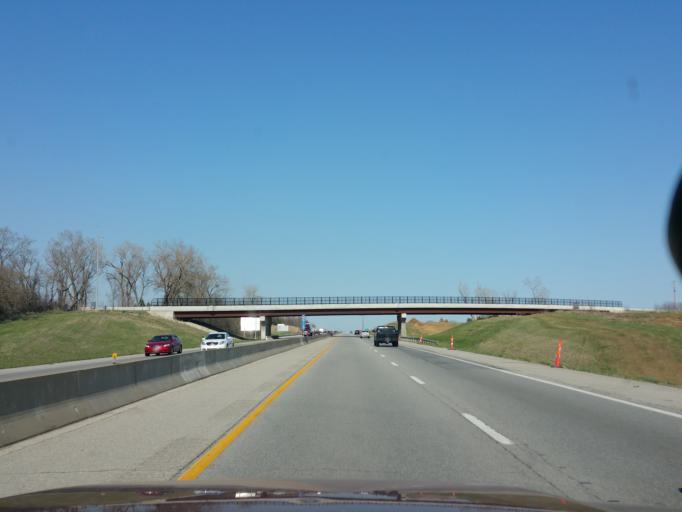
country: US
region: Kansas
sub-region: Wyandotte County
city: Bonner Springs
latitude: 39.1004
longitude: -94.8664
